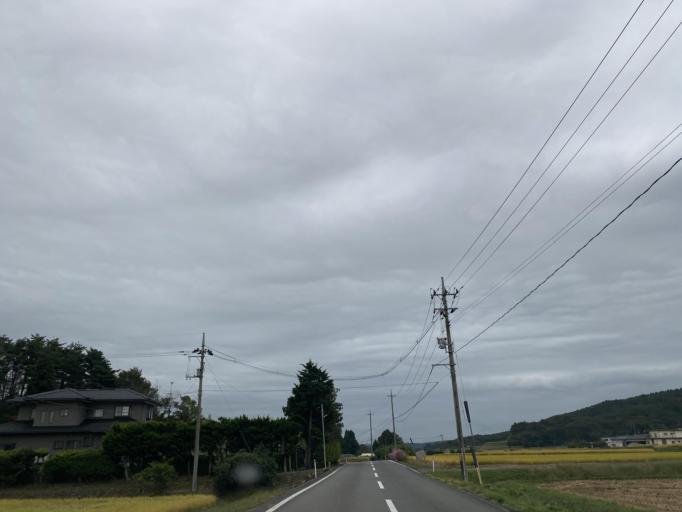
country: JP
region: Fukushima
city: Koriyama
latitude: 37.3600
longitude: 140.2599
